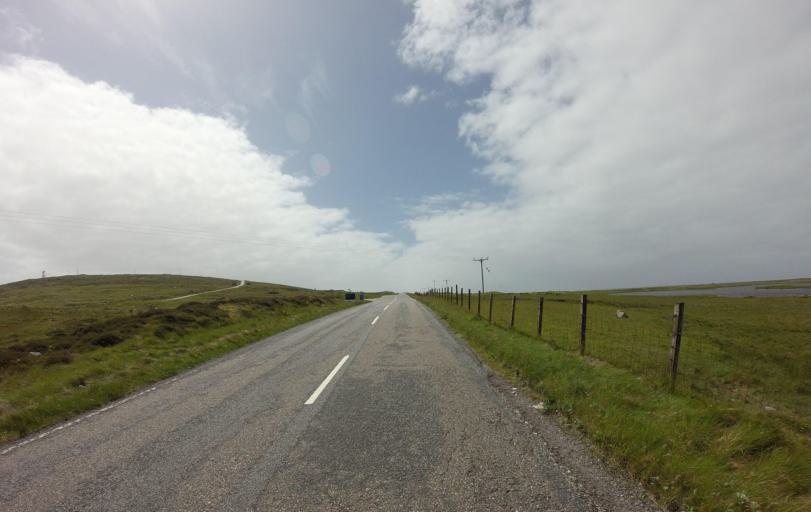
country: GB
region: Scotland
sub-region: Eilean Siar
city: Benbecula
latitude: 57.3485
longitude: -7.3593
